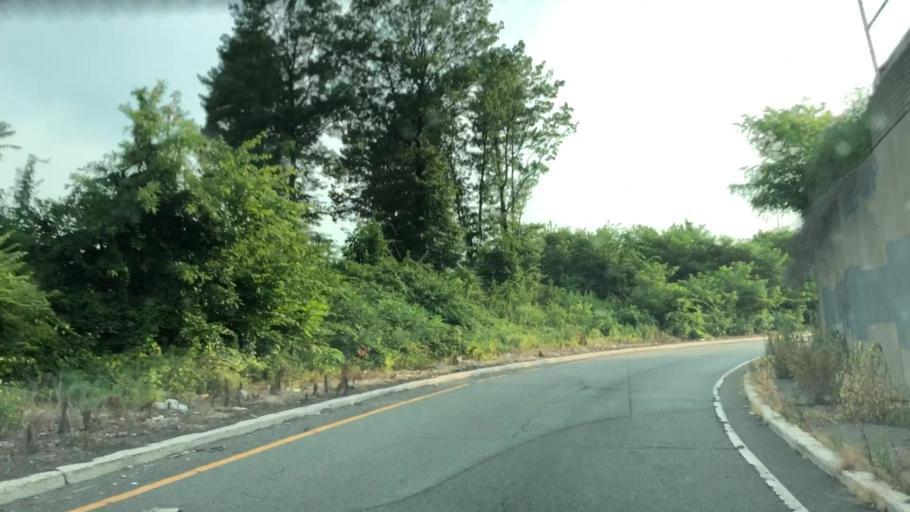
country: US
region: New Jersey
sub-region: Bergen County
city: Lyndhurst
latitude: 40.8265
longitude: -74.1239
